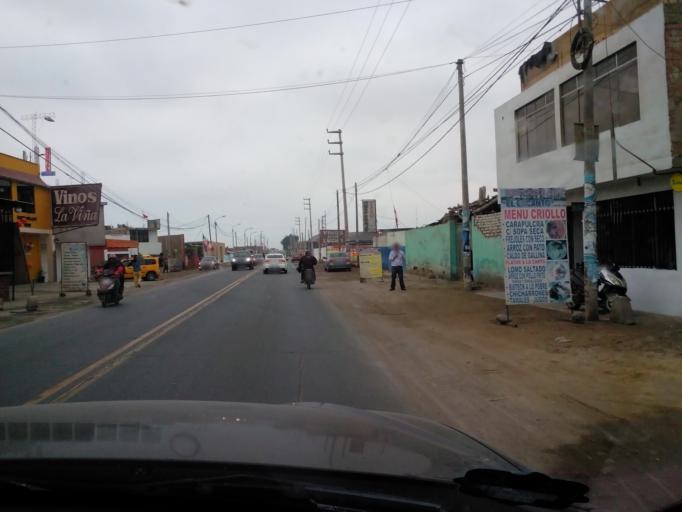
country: PE
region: Ica
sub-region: Provincia de Chincha
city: San Pedro
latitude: -13.4131
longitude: -76.1524
